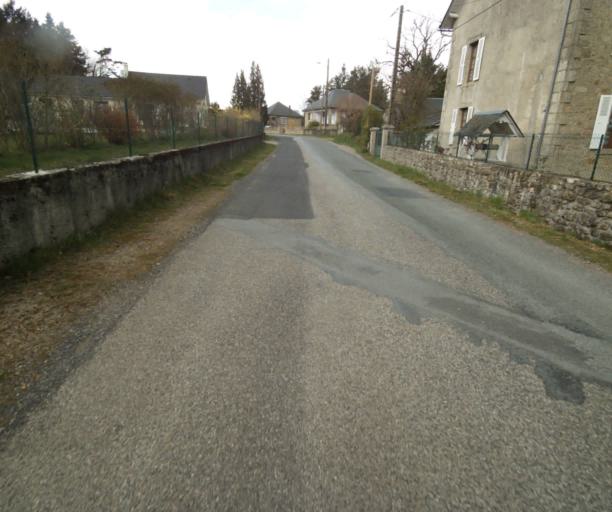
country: FR
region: Limousin
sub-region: Departement de la Correze
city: Correze
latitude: 45.2799
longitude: 1.9766
